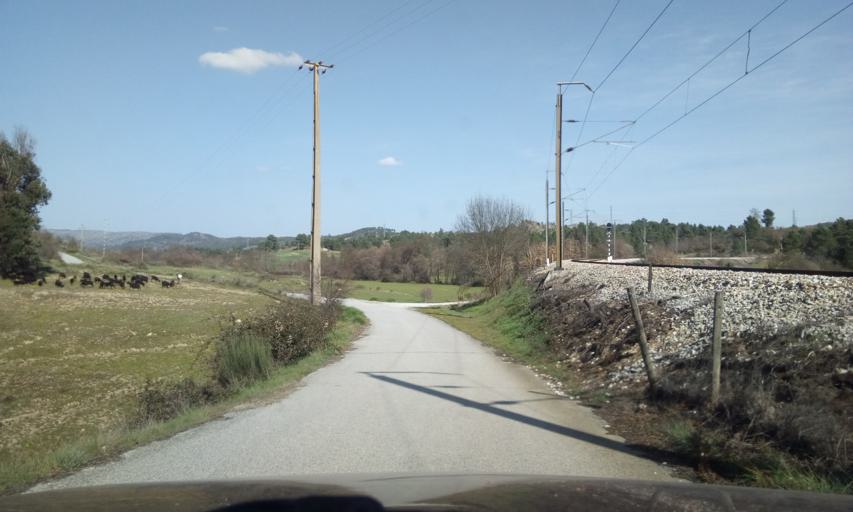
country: PT
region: Guarda
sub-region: Celorico da Beira
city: Celorico da Beira
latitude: 40.6428
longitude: -7.4294
